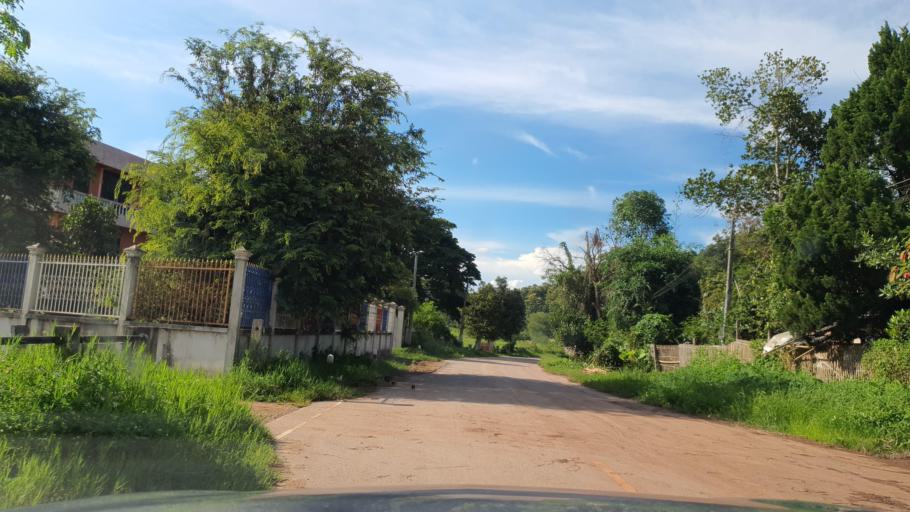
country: TH
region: Chiang Mai
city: Mae On
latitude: 18.7383
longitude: 99.3031
